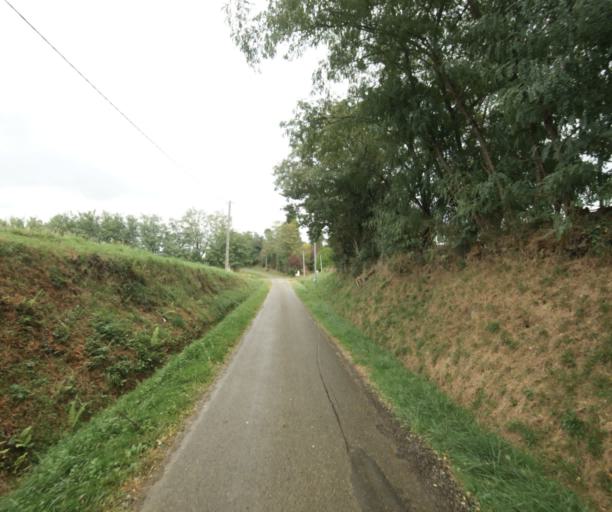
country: FR
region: Midi-Pyrenees
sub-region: Departement du Gers
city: Cazaubon
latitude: 43.8964
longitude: -0.1051
